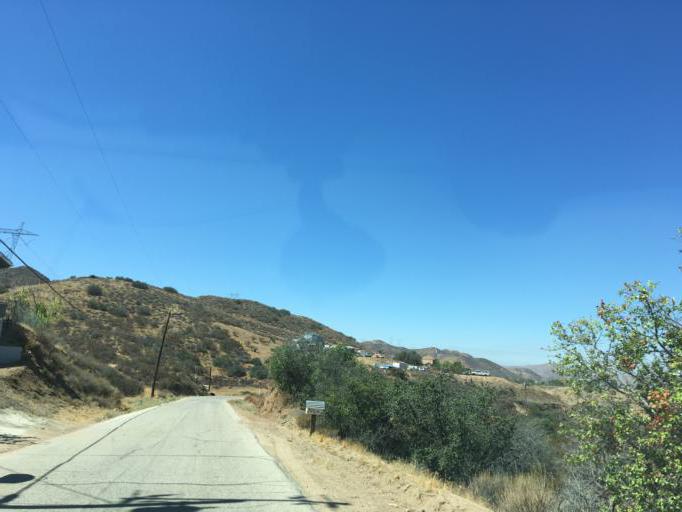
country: US
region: California
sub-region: Los Angeles County
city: Agua Dulce
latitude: 34.5200
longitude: -118.3277
